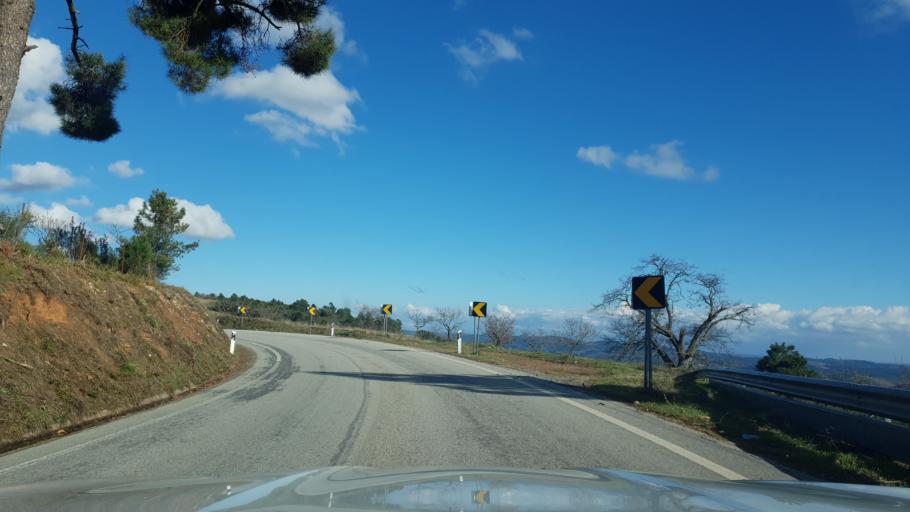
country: PT
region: Braganca
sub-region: Torre de Moncorvo
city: Torre de Moncorvo
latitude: 41.1792
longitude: -6.9342
